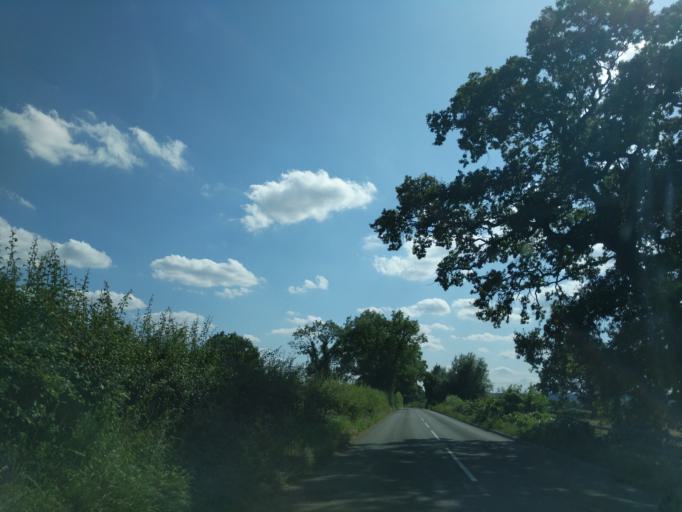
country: GB
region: England
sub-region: Staffordshire
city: Rugeley
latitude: 52.7962
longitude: -1.9328
